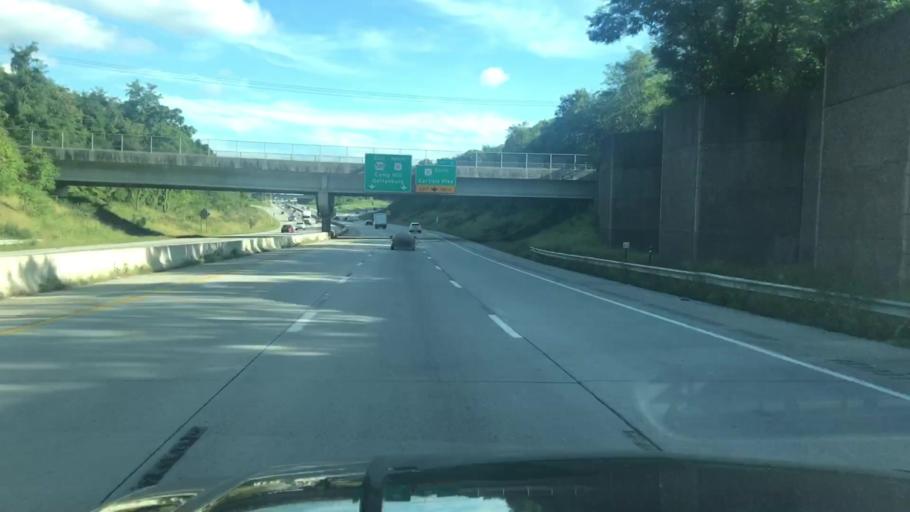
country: US
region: Pennsylvania
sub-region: Cumberland County
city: Mechanicsburg
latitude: 40.2530
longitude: -76.9903
